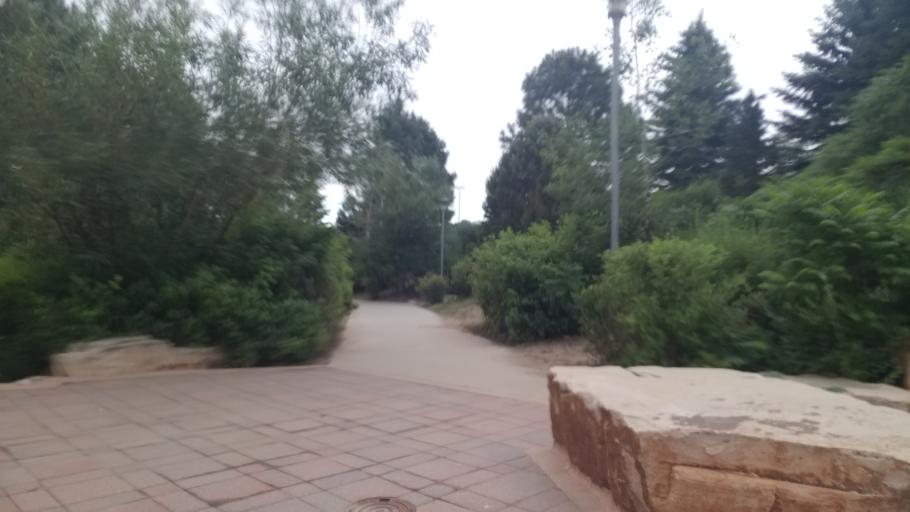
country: US
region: Colorado
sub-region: Boulder County
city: Superior
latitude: 39.9336
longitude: -105.1320
